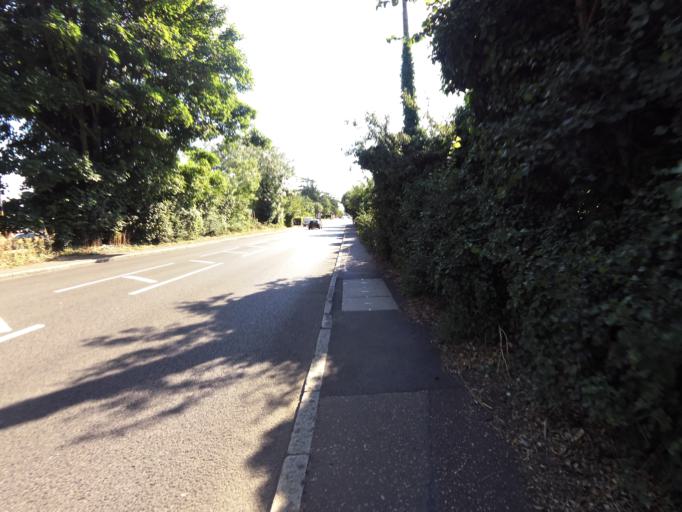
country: GB
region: England
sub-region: Essex
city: Witham
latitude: 51.8040
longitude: 0.6458
